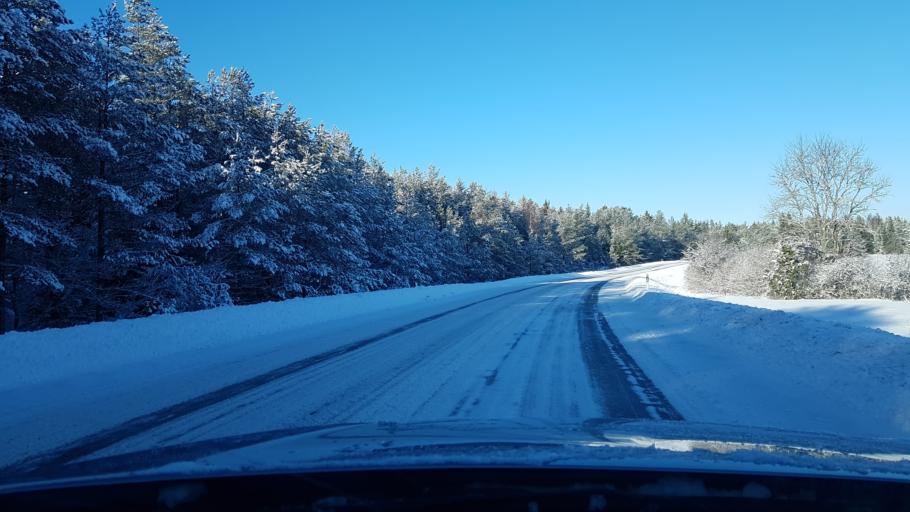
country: EE
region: Hiiumaa
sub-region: Kaerdla linn
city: Kardla
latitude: 58.9466
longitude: 22.7719
